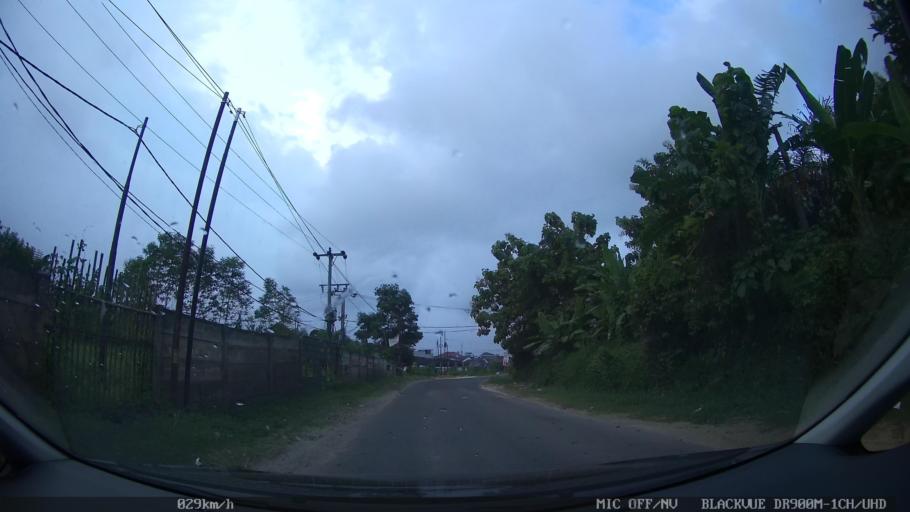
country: ID
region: Lampung
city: Bandarlampung
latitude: -5.4225
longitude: 105.2806
